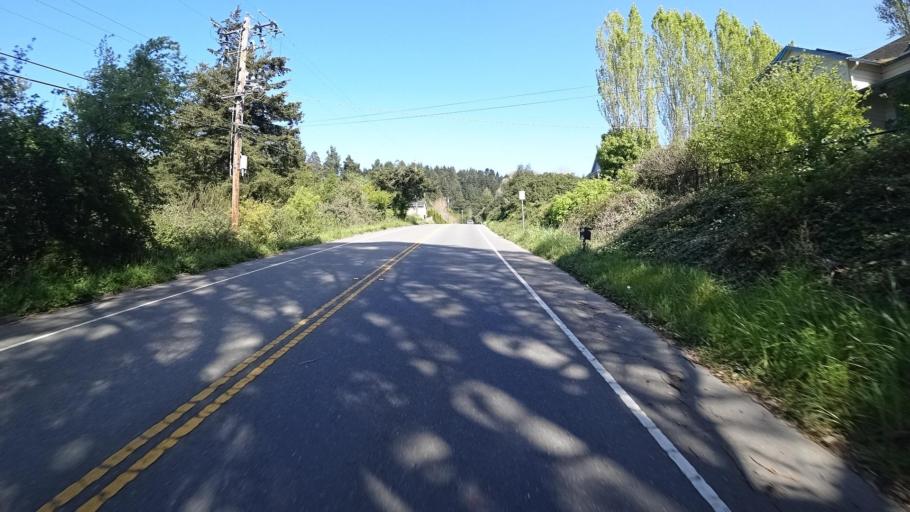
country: US
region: California
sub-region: Humboldt County
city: Hydesville
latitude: 40.5703
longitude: -124.1256
